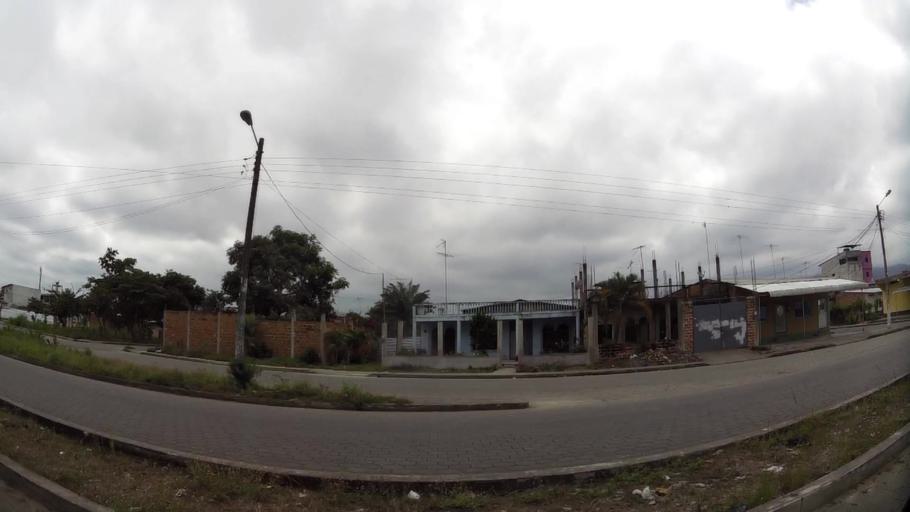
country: EC
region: Guayas
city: Naranjal
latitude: -2.6800
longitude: -79.6240
